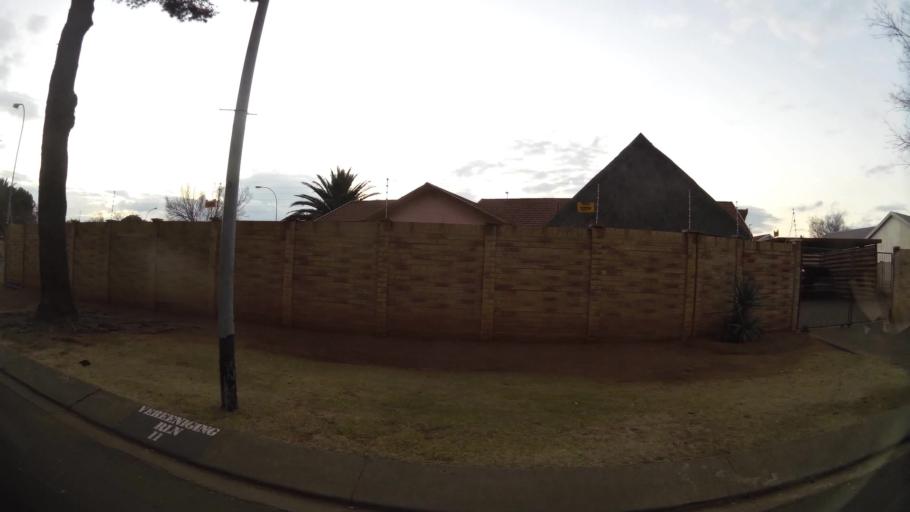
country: ZA
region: Orange Free State
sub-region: Mangaung Metropolitan Municipality
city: Bloemfontein
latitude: -29.1677
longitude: 26.1944
